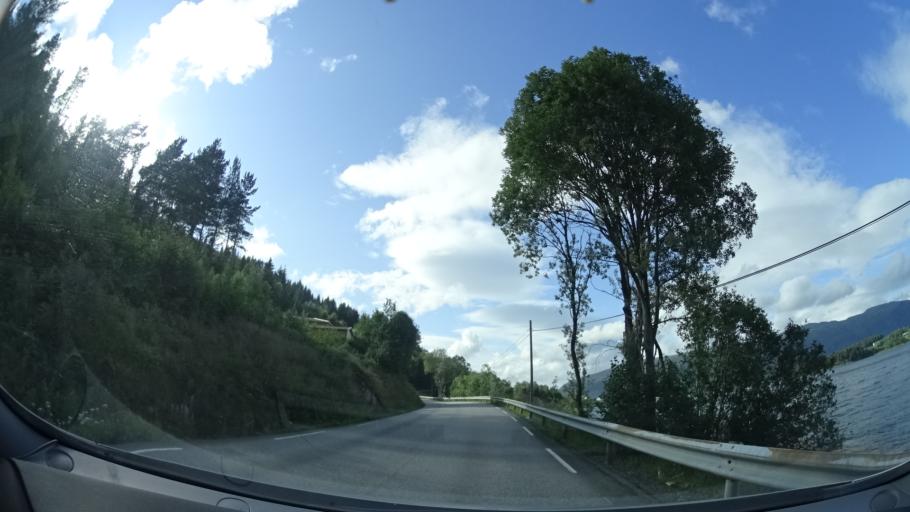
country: NO
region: More og Romsdal
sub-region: Aure
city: Aure
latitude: 63.1311
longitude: 8.5060
